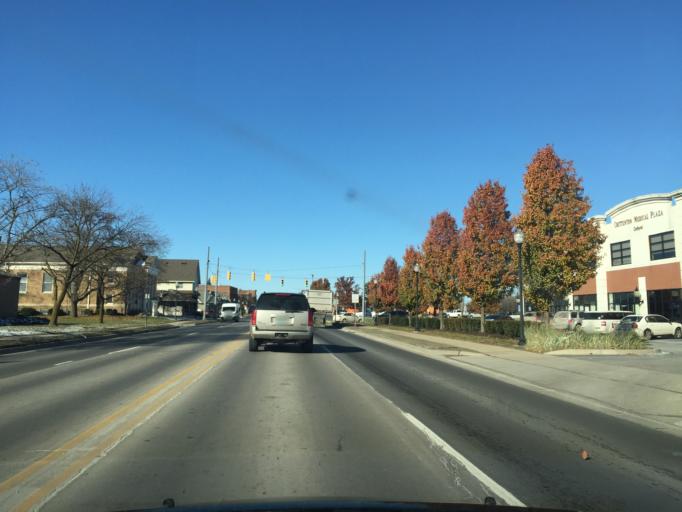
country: US
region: Michigan
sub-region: Oakland County
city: Oxford
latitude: 42.8219
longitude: -83.2623
